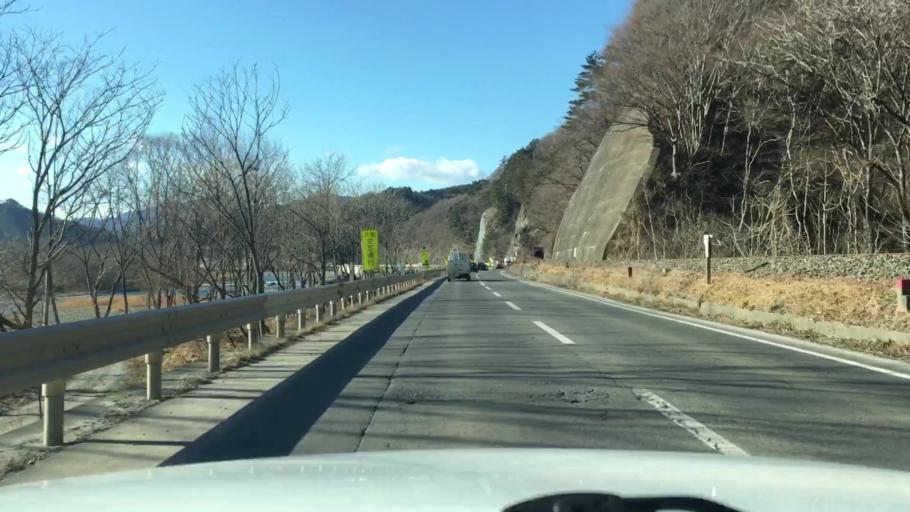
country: JP
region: Iwate
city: Miyako
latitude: 39.6313
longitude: 141.8724
